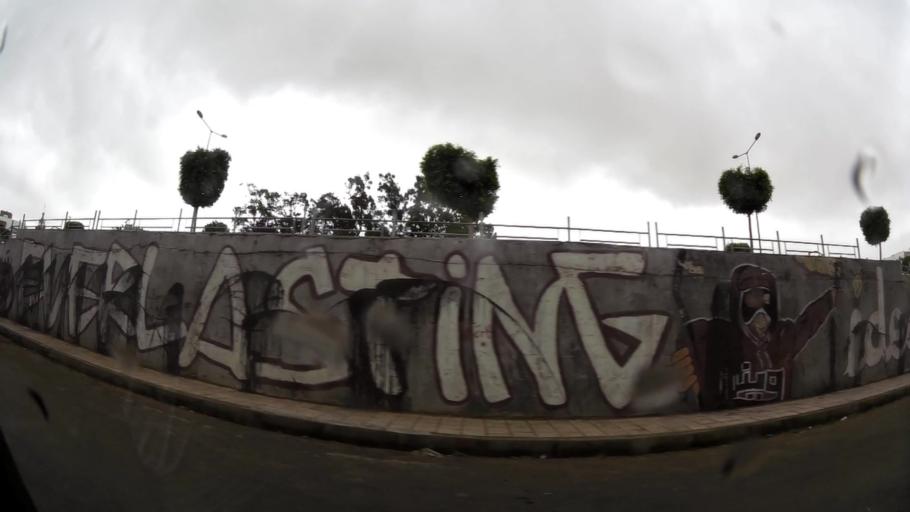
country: MA
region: Grand Casablanca
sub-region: Mediouna
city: Tit Mellil
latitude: 33.6194
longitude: -7.4841
